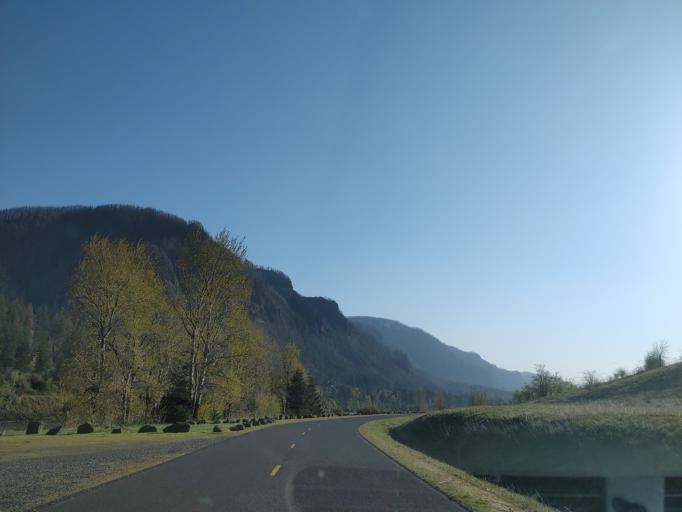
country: US
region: Oregon
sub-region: Hood River County
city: Cascade Locks
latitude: 45.6309
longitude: -121.9720
